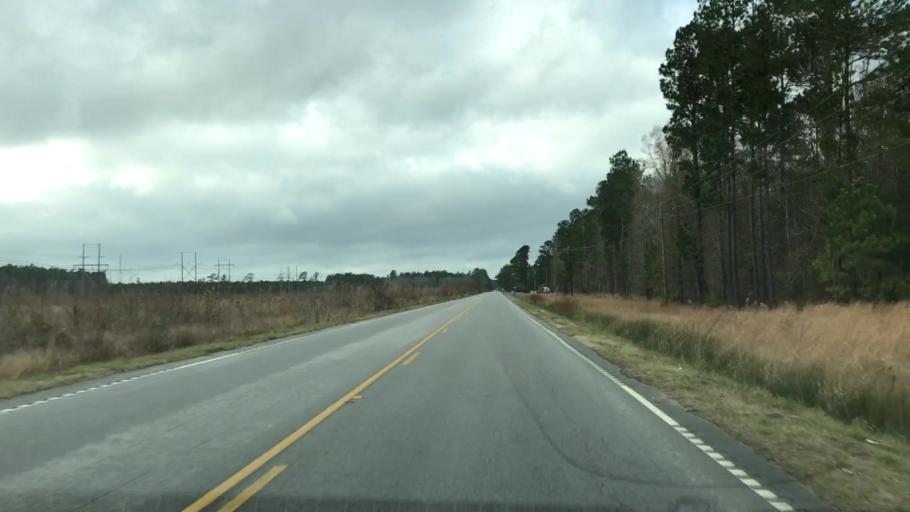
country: US
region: South Carolina
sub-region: Berkeley County
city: Saint Stephen
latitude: 33.2818
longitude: -79.7332
